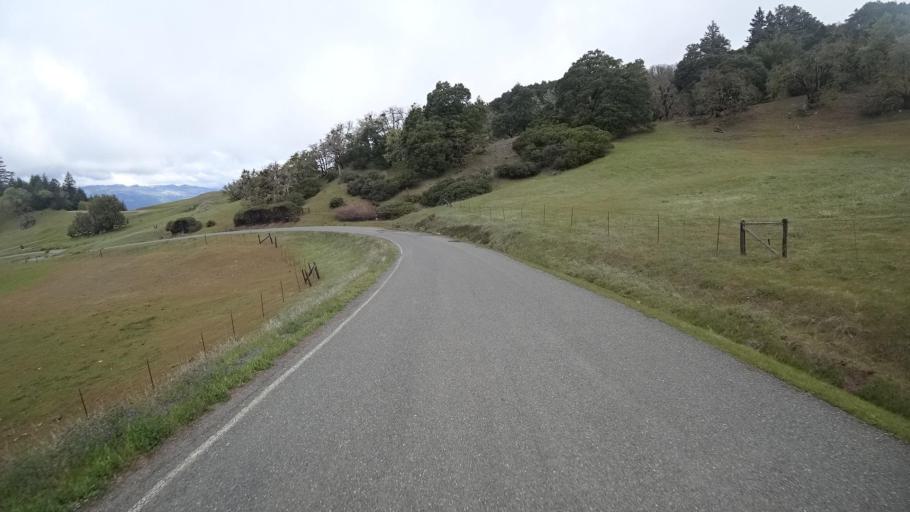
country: US
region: California
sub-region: Humboldt County
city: Redway
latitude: 40.1571
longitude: -123.5490
